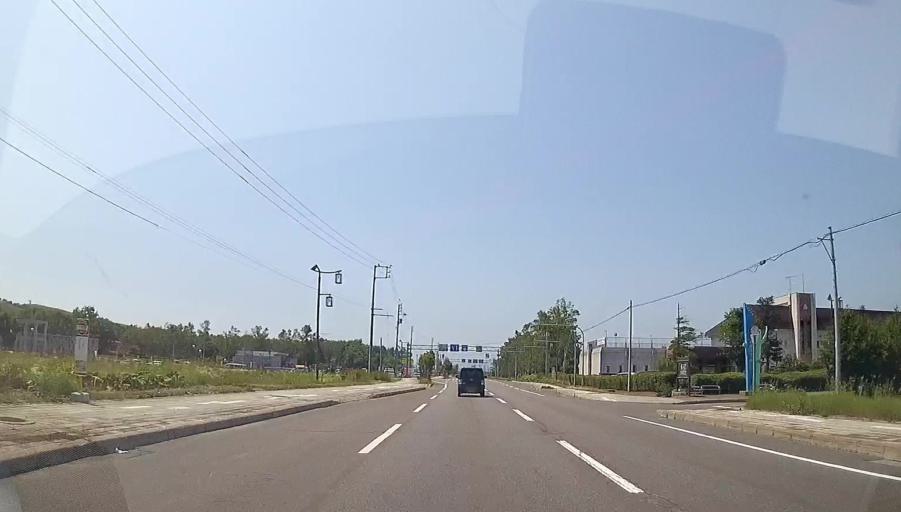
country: JP
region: Hokkaido
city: Obihiro
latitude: 42.5606
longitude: 143.2997
